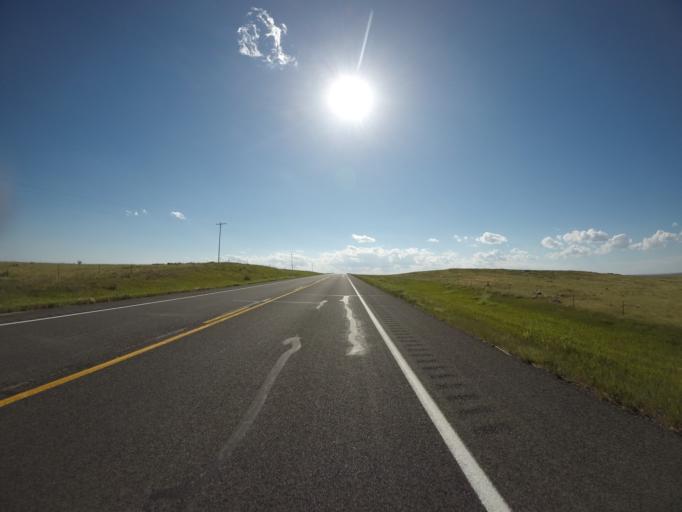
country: US
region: Colorado
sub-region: Morgan County
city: Brush
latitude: 40.6103
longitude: -103.6426
